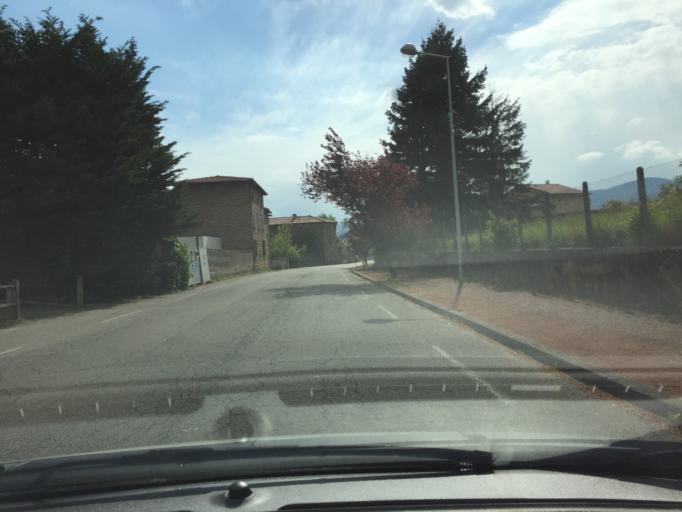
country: FR
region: Rhone-Alpes
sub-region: Departement du Rhone
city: Mornant
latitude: 45.6420
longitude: 4.6899
